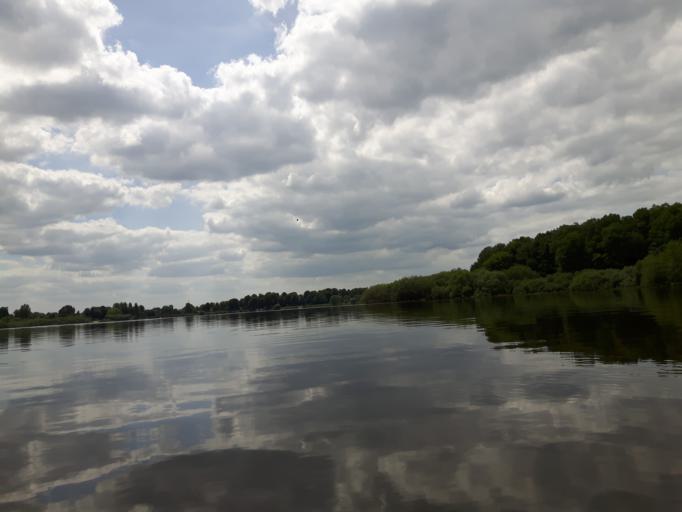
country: DE
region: Schleswig-Holstein
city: Muhbrook
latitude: 54.1388
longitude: 9.9946
